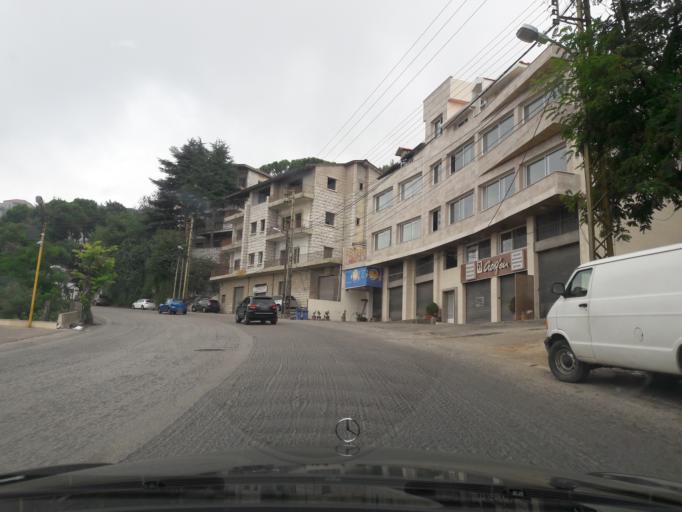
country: LB
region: Mont-Liban
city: Djounie
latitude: 33.9178
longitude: 35.6653
